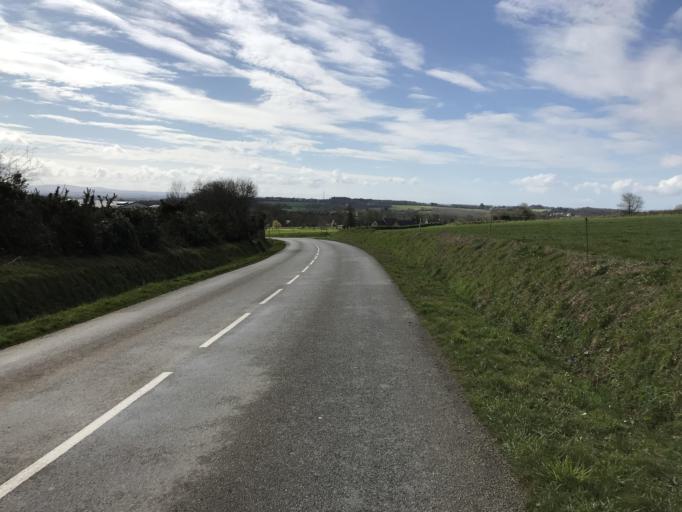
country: FR
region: Brittany
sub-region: Departement du Finistere
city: Dirinon
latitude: 48.3920
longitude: -4.2663
